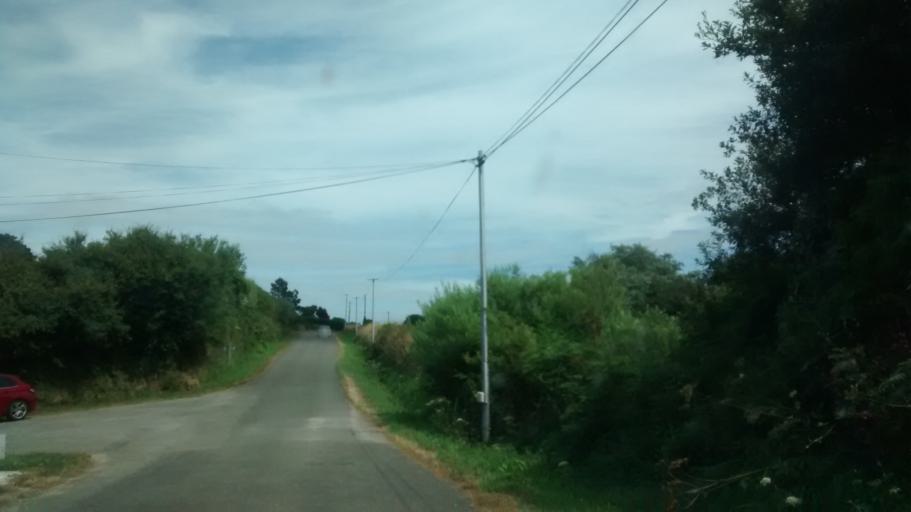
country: FR
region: Brittany
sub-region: Departement du Finistere
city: Plouguerneau
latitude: 48.6223
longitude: -4.4749
